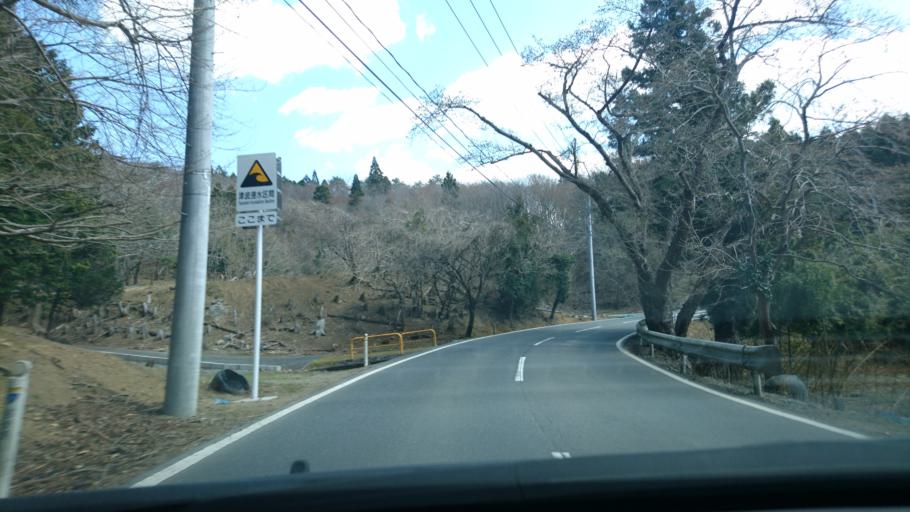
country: JP
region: Miyagi
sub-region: Oshika Gun
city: Onagawa Cho
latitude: 38.4730
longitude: 141.4856
